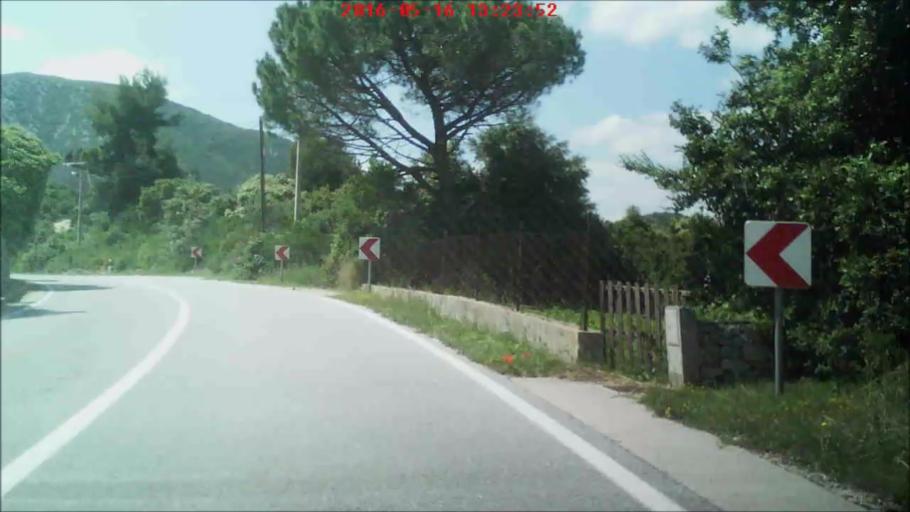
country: HR
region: Dubrovacko-Neretvanska
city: Ston
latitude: 42.8445
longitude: 17.7087
